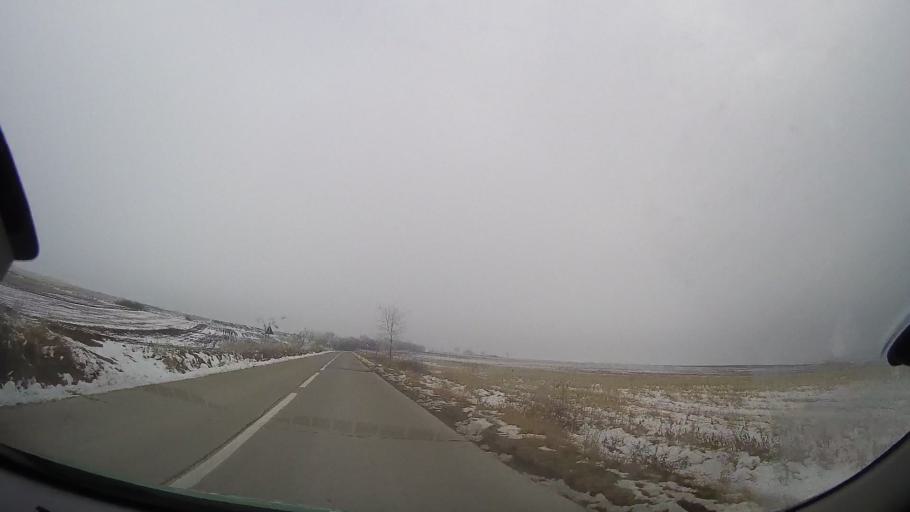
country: RO
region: Vaslui
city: Coroiesti
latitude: 46.2138
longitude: 27.4751
